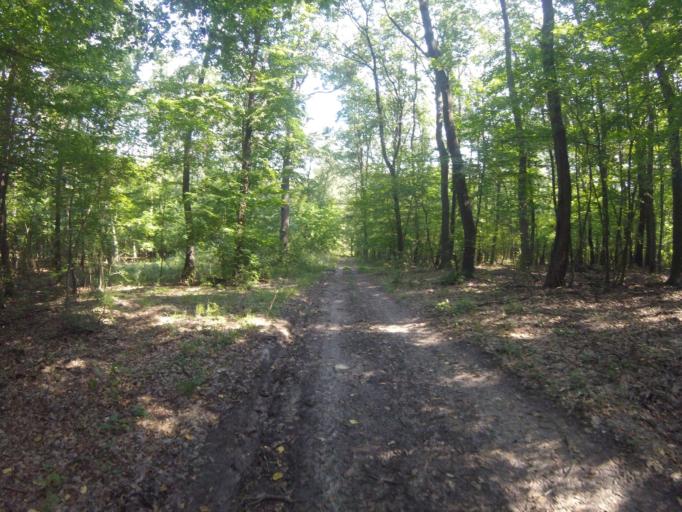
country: HU
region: Nograd
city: Bujak
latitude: 47.8946
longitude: 19.5284
